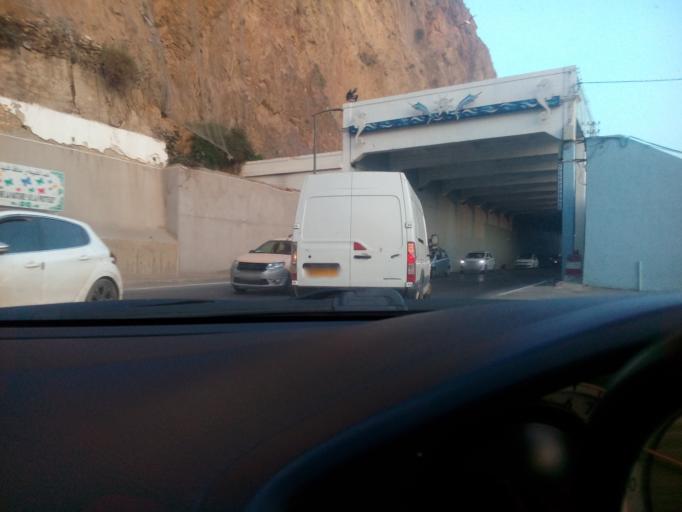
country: DZ
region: Oran
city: Oran
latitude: 35.7096
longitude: -0.6571
